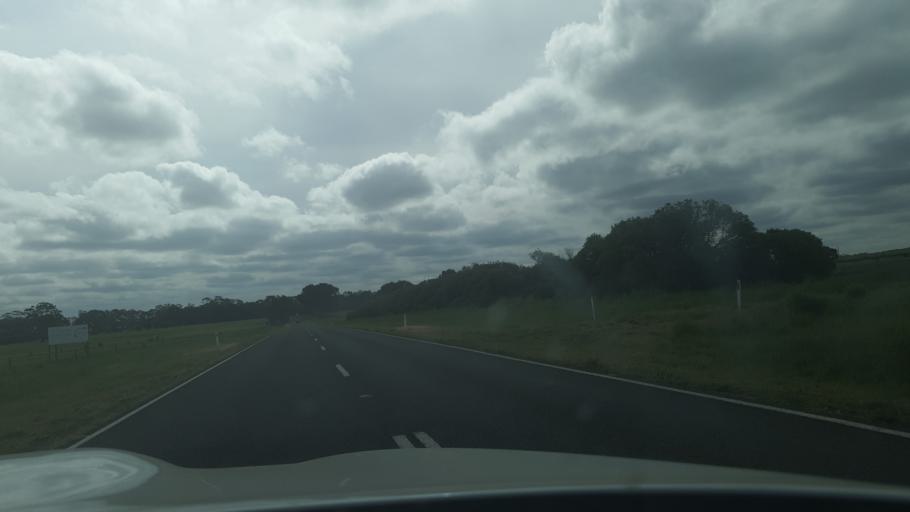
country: AU
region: Victoria
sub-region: Central Goldfields
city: Maryborough
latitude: -37.2068
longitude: 143.7157
